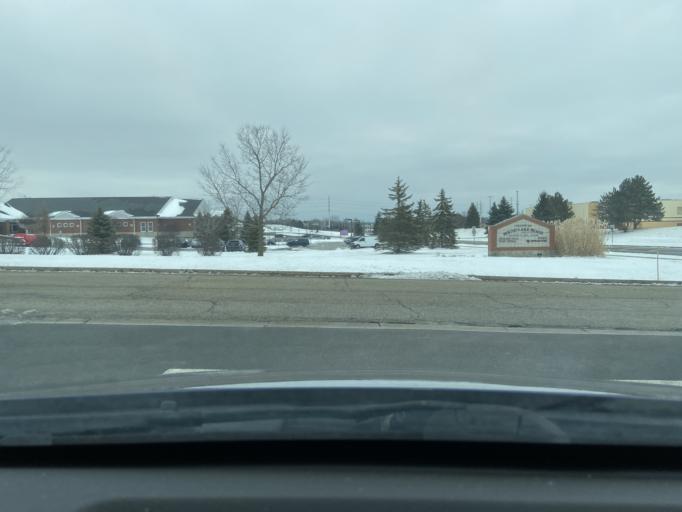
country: US
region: Illinois
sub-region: Lake County
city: Round Lake Beach
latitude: 42.3828
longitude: -88.0712
